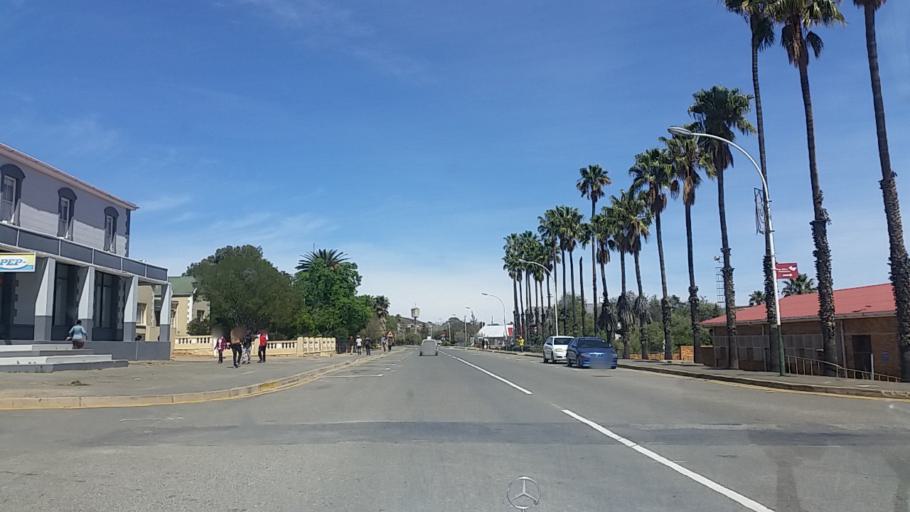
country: ZA
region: Western Cape
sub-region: Eden District Municipality
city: Knysna
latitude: -33.6563
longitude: 23.1271
